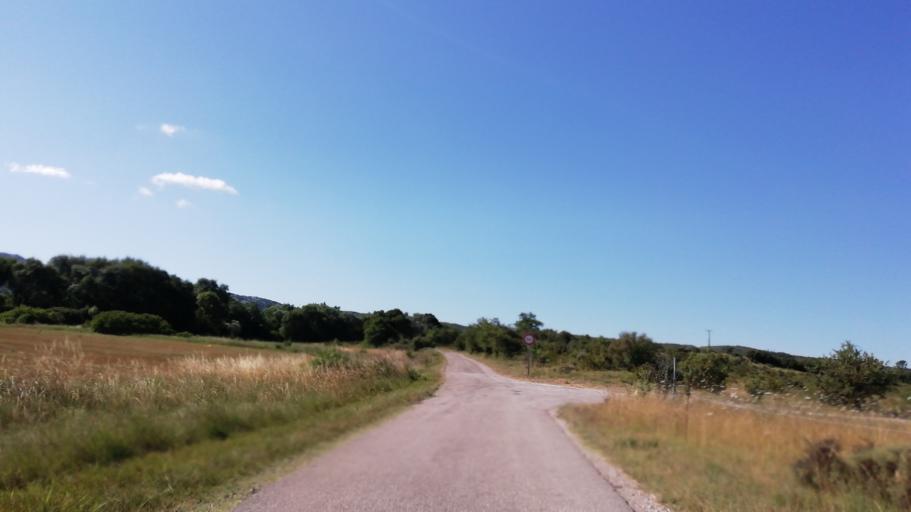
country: FR
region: Languedoc-Roussillon
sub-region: Departement de l'Herault
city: Saint-Martin-de-Londres
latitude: 43.7988
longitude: 3.7600
